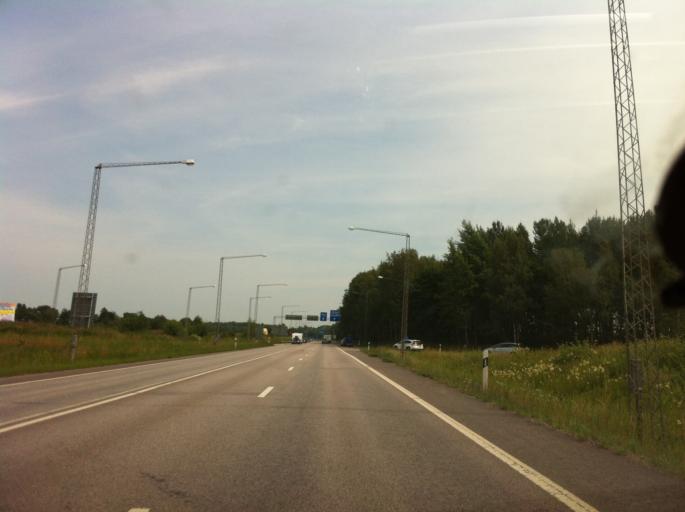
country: SE
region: Kalmar
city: Faerjestaden
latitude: 56.6665
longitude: 16.4814
